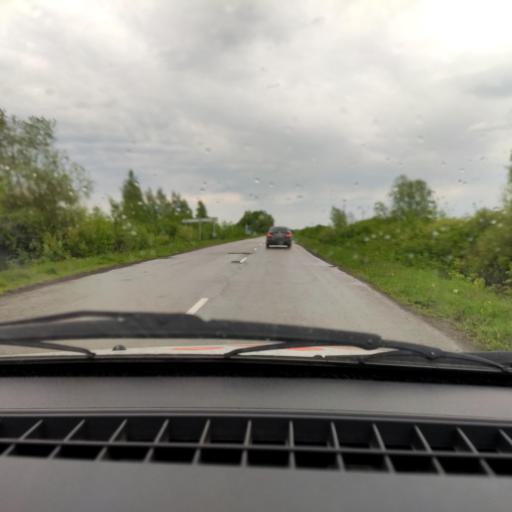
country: RU
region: Bashkortostan
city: Kudeyevskiy
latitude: 54.8329
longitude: 56.7928
